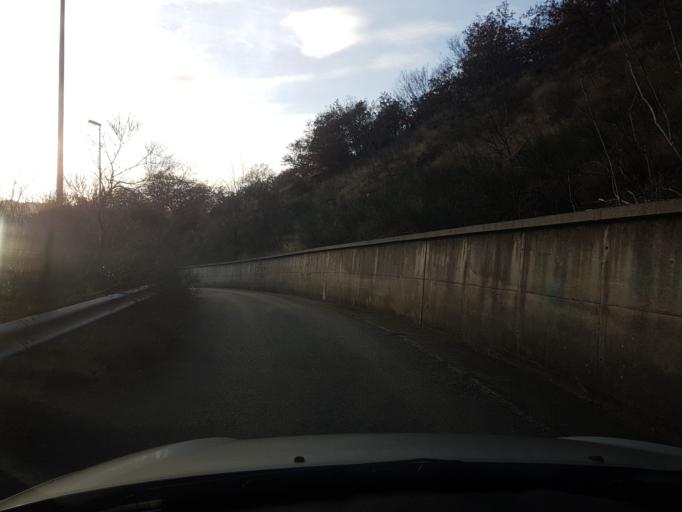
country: IT
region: Friuli Venezia Giulia
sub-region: Provincia di Trieste
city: Domio
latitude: 45.6100
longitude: 13.8387
